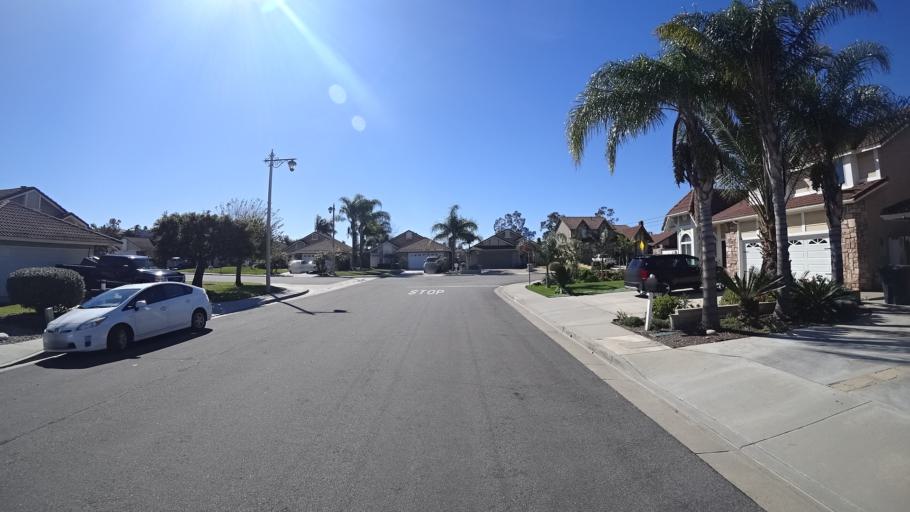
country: US
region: California
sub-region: Orange County
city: Yorba Linda
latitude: 33.8617
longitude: -117.7529
